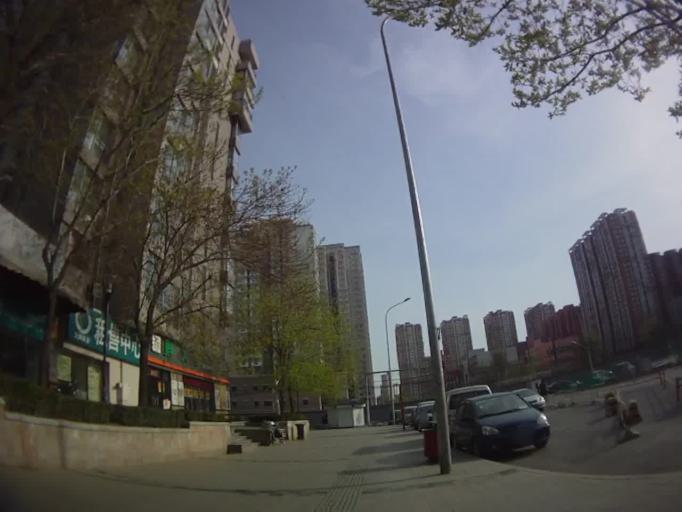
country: CN
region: Beijing
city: Longtan
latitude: 39.8938
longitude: 116.4444
